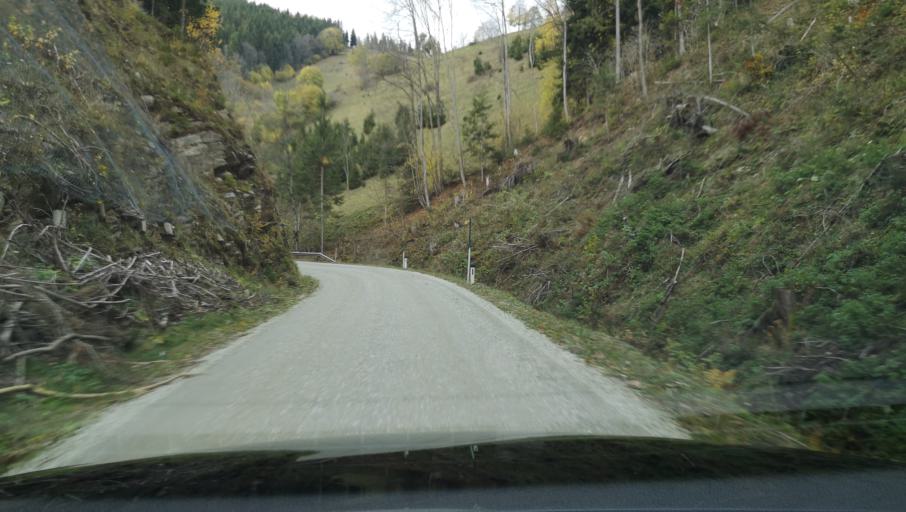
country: AT
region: Styria
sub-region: Politischer Bezirk Weiz
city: Gasen
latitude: 47.3773
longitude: 15.6270
